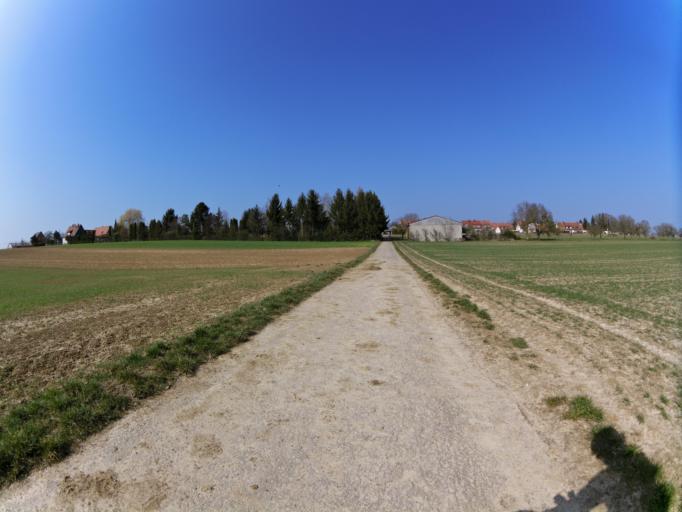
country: DE
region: Bavaria
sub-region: Regierungsbezirk Unterfranken
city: Geroldshausen
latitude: 49.6821
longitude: 9.9077
